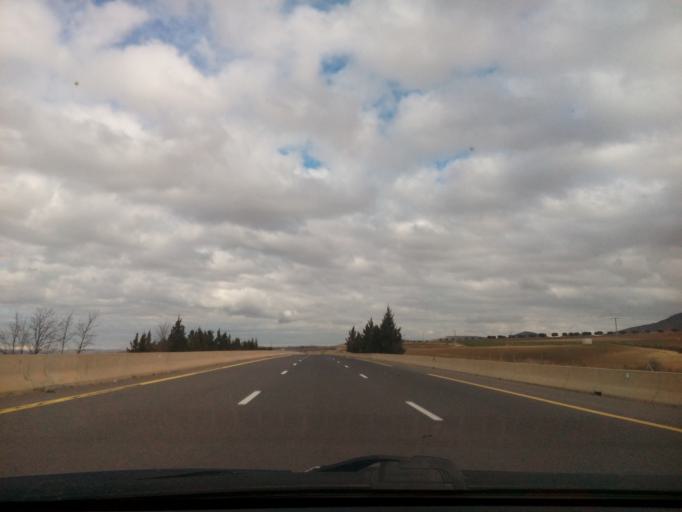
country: DZ
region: Tlemcen
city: Bensekrane
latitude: 34.9998
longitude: -1.1922
